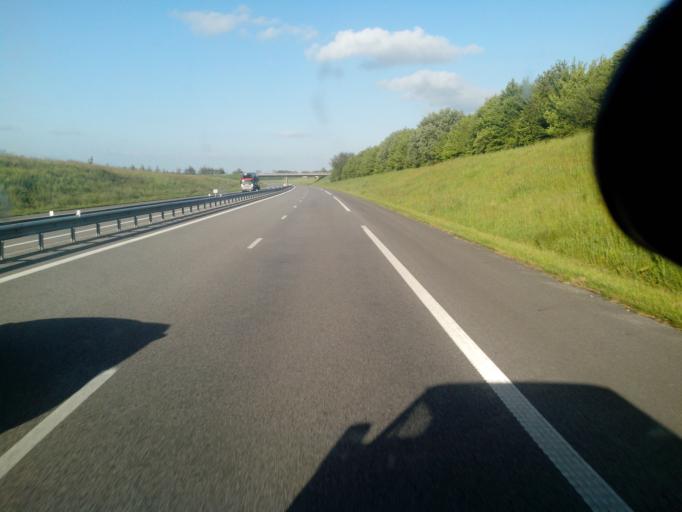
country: FR
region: Haute-Normandie
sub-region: Departement de la Seine-Maritime
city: Yerville
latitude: 49.6567
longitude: 0.8954
